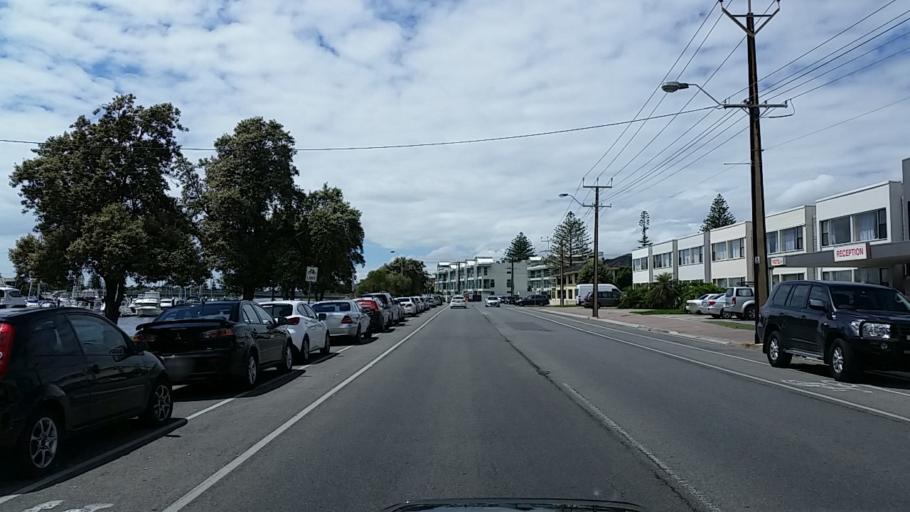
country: AU
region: South Australia
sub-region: Adelaide
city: Glenelg
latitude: -34.9748
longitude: 138.5142
